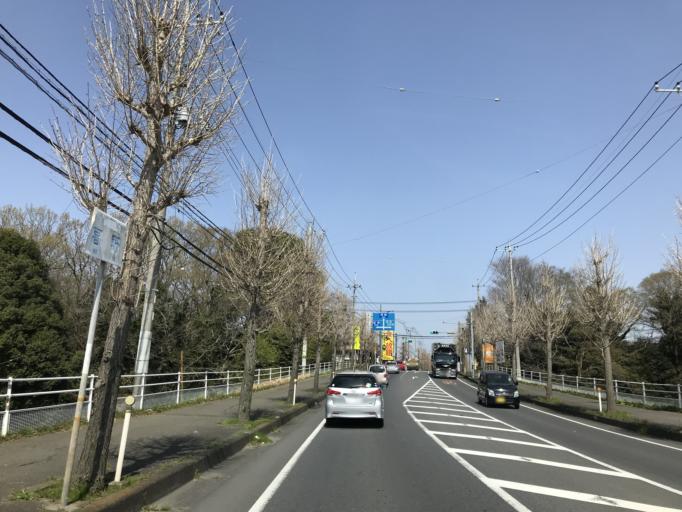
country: JP
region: Ibaraki
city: Moriya
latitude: 35.9262
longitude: 139.9975
